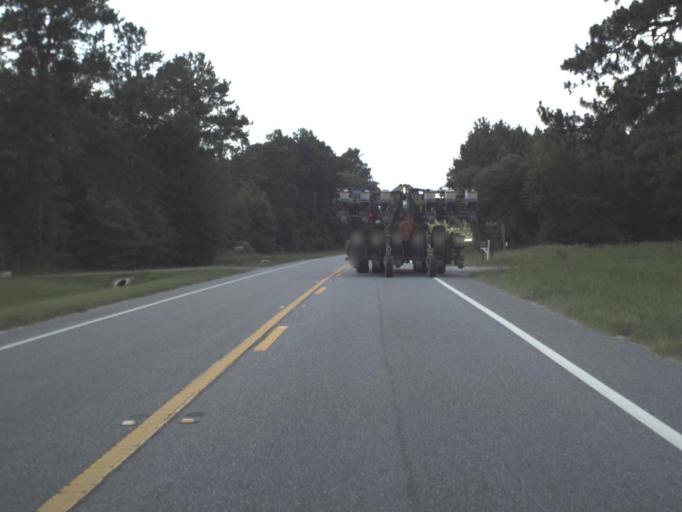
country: US
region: Georgia
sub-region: Echols County
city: Statenville
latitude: 30.5830
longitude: -83.0895
